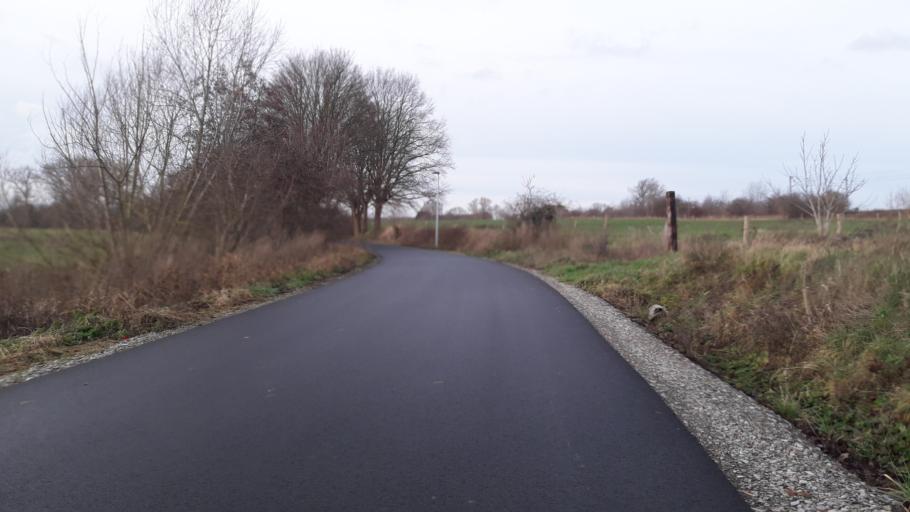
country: DE
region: North Rhine-Westphalia
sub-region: Regierungsbezirk Arnsberg
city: Soest
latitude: 51.5855
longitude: 8.0697
